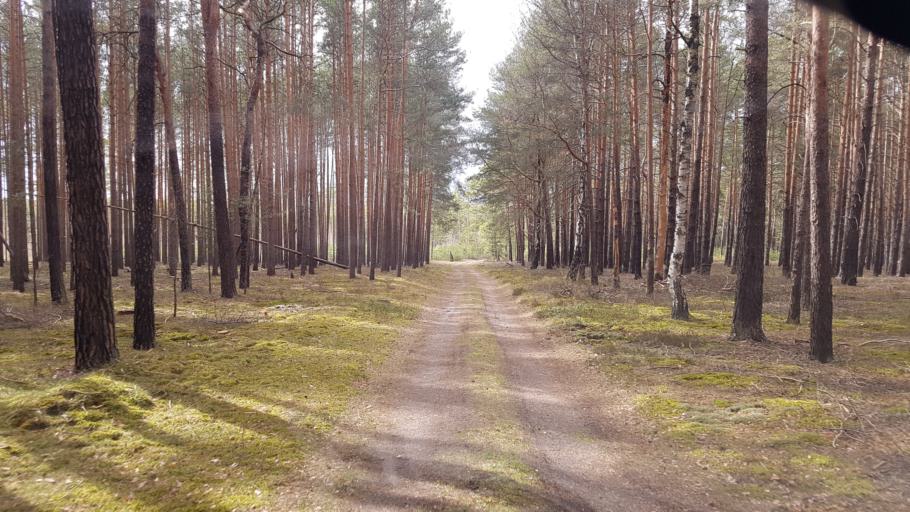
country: DE
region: Brandenburg
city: Finsterwalde
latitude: 51.5668
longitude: 13.6859
